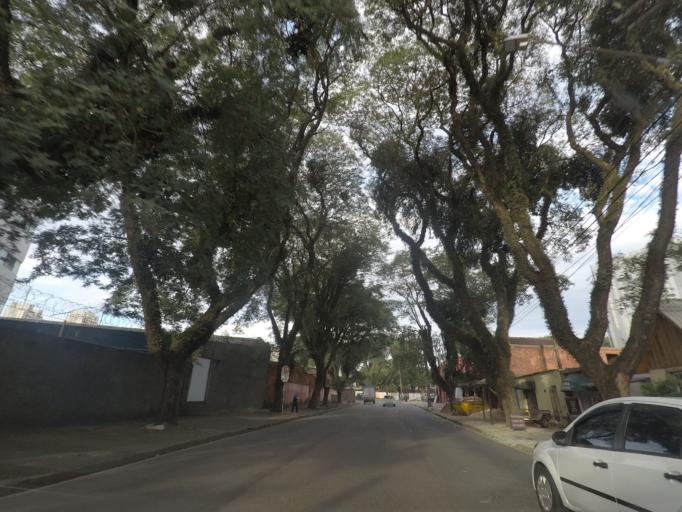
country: BR
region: Parana
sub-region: Curitiba
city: Curitiba
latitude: -25.4757
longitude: -49.2947
